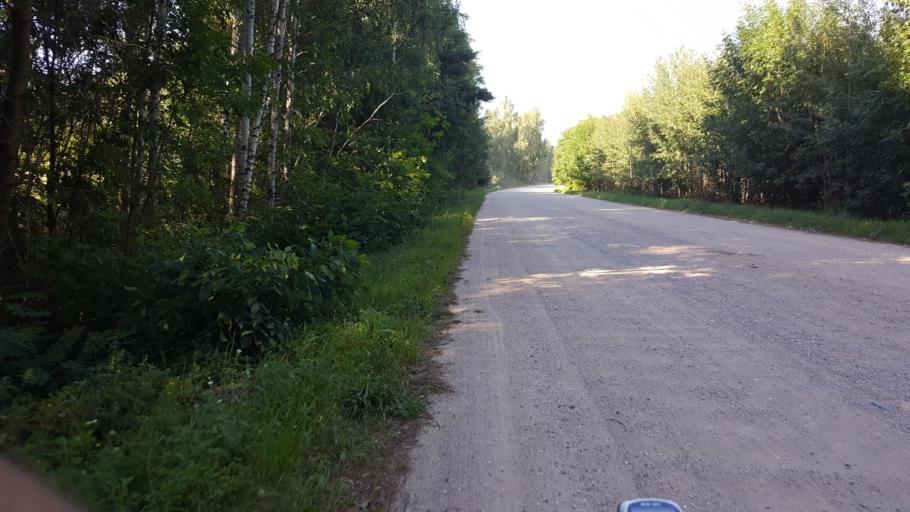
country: BY
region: Brest
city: Kamyanyets
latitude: 52.3700
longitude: 23.7286
